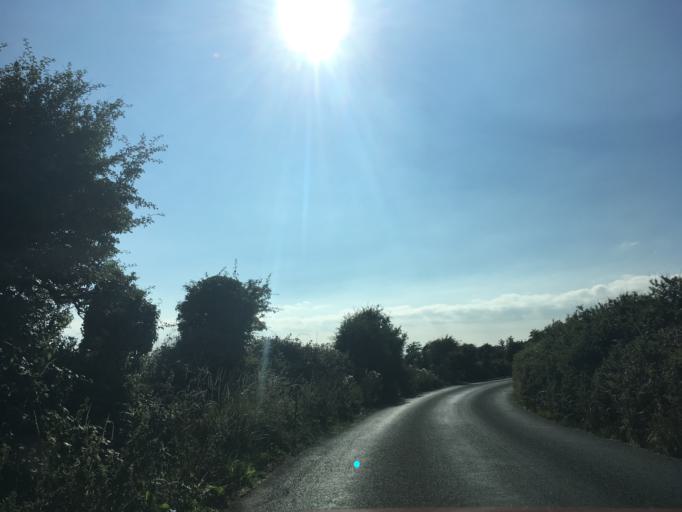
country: IE
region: Leinster
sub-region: Loch Garman
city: Rosslare
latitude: 52.2252
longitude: -6.4481
